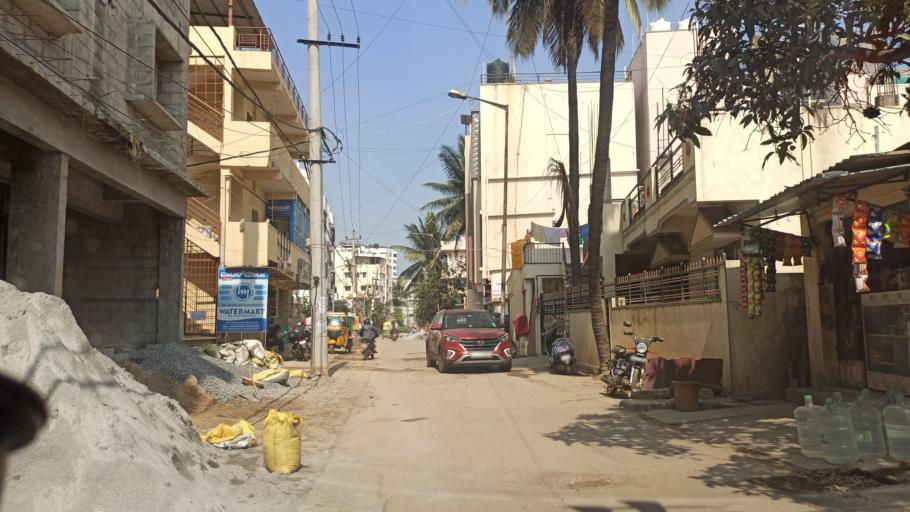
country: IN
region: Karnataka
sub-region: Bangalore Urban
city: Bangalore
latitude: 12.9540
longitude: 77.7077
